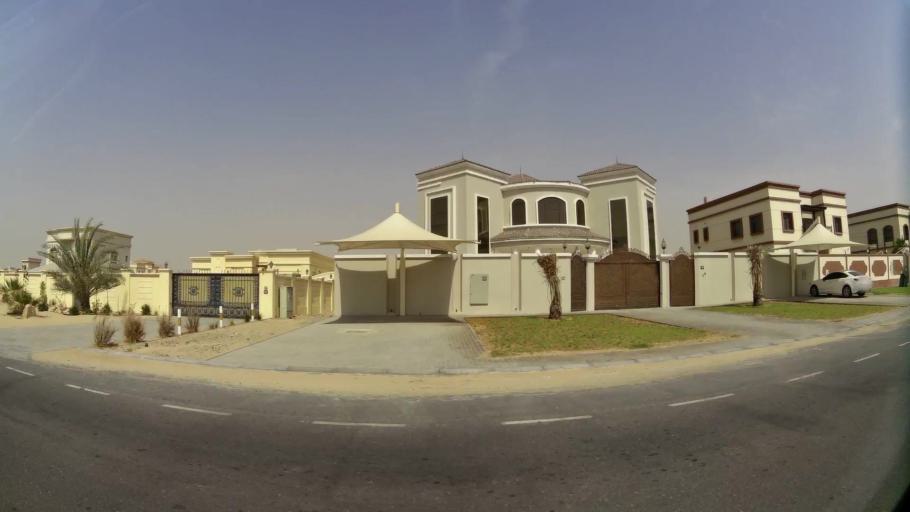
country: AE
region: Ash Shariqah
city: Sharjah
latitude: 25.2531
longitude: 55.4862
